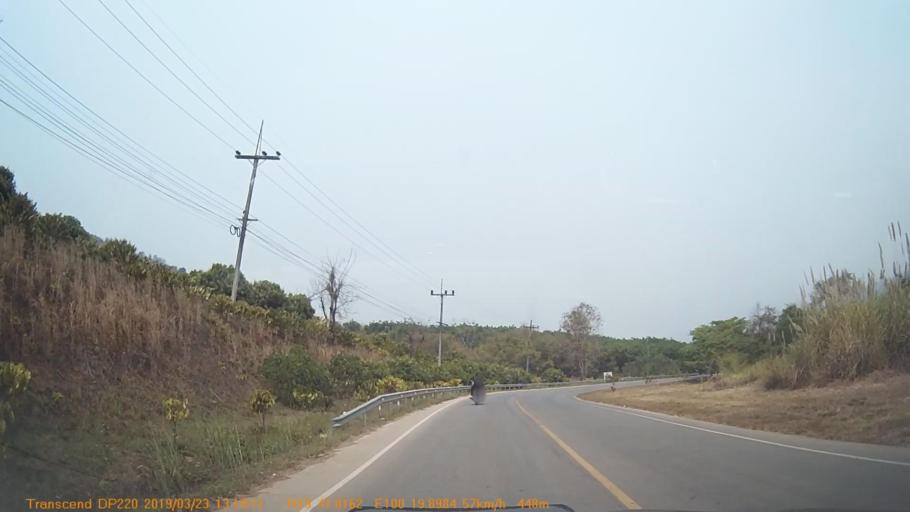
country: TH
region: Chiang Rai
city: Khun Tan
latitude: 19.7839
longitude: 100.3318
